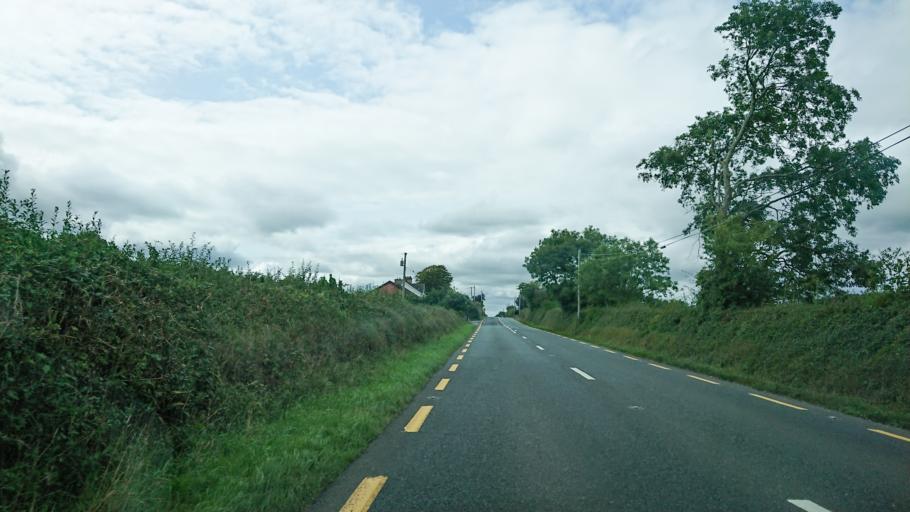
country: IE
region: Munster
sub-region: Waterford
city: Dungarvan
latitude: 52.1147
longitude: -7.7142
